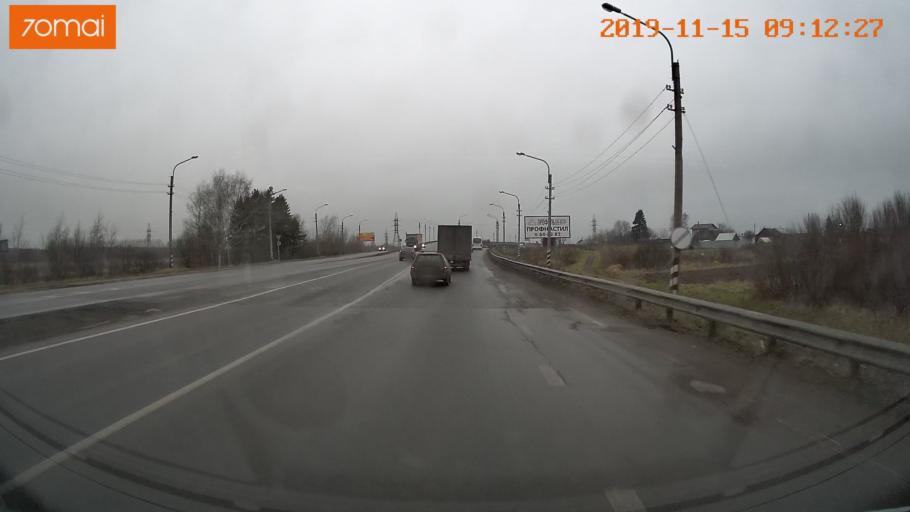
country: RU
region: Vologda
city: Tonshalovo
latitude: 59.2082
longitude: 37.9369
